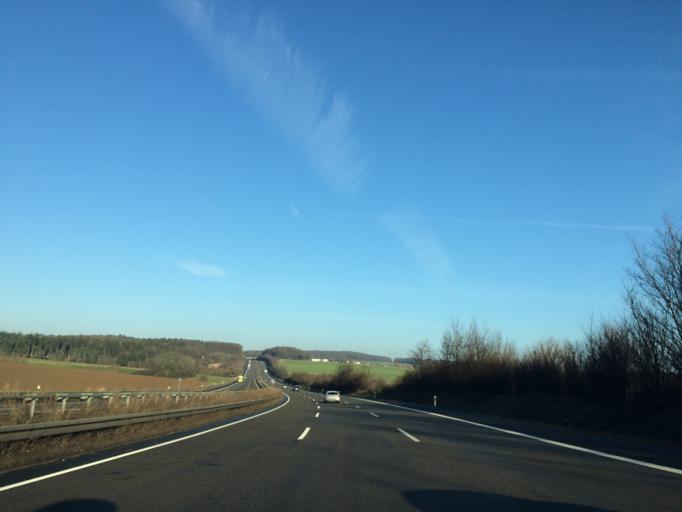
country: DE
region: Hesse
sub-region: Regierungsbezirk Kassel
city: Malsfeld
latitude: 51.0480
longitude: 9.4973
